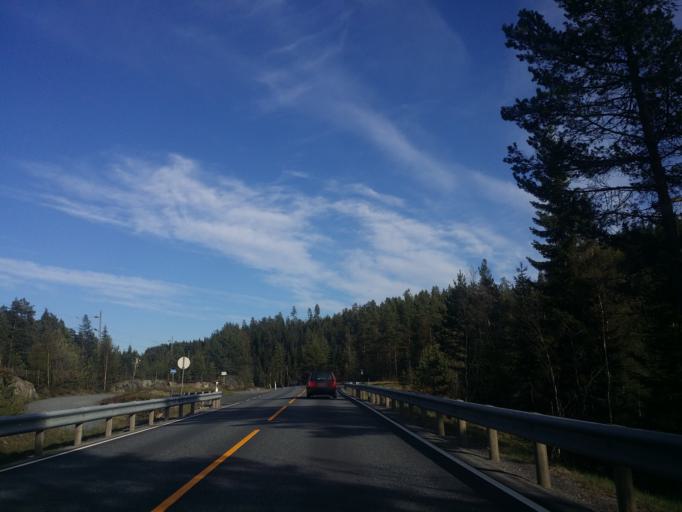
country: NO
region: Buskerud
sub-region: Kongsberg
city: Kongsberg
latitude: 59.6299
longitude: 9.5422
